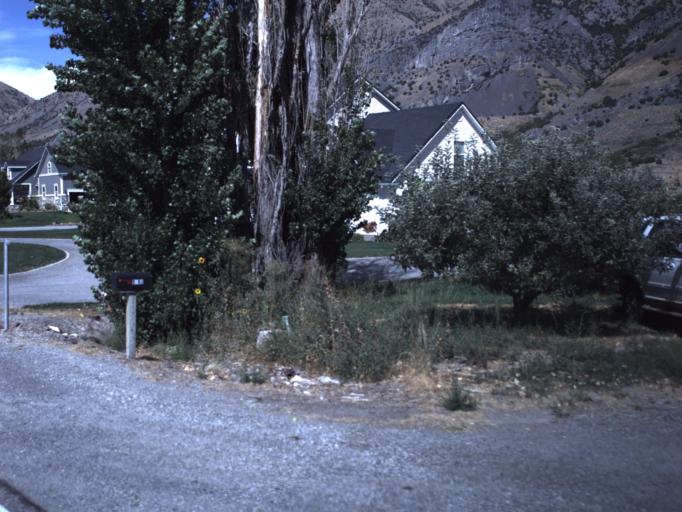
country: US
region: Utah
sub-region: Box Elder County
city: Honeyville
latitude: 41.6879
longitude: -112.0899
